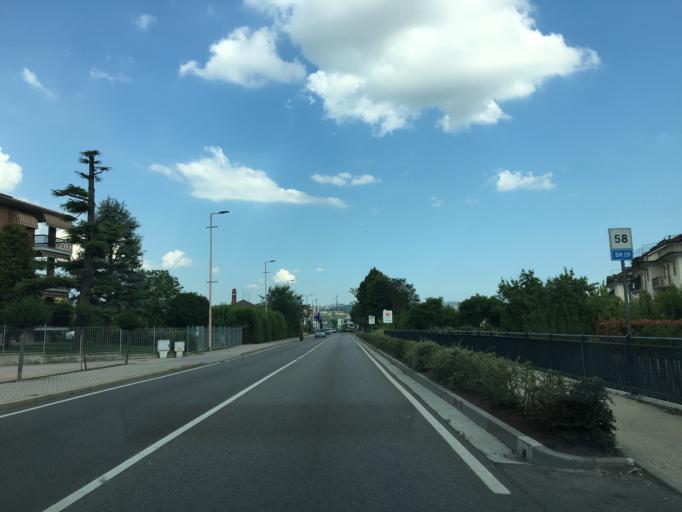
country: IT
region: Piedmont
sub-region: Provincia di Cuneo
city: Mussotto
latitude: 44.7136
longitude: 8.0195
